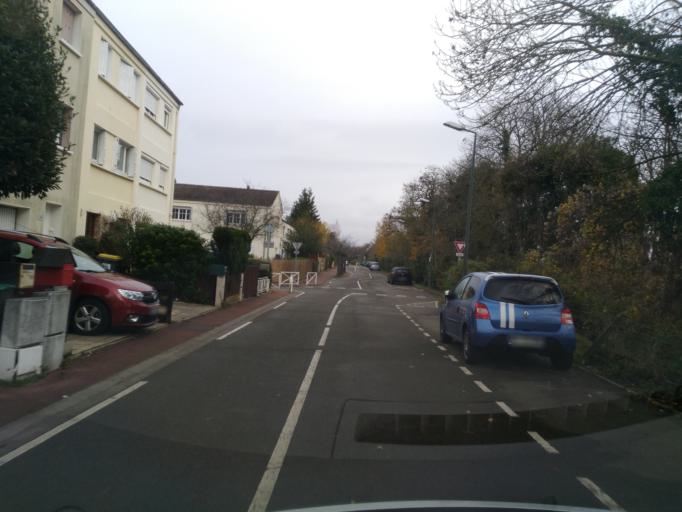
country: FR
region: Ile-de-France
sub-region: Departement des Yvelines
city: Villepreux
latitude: 48.8239
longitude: 2.0021
